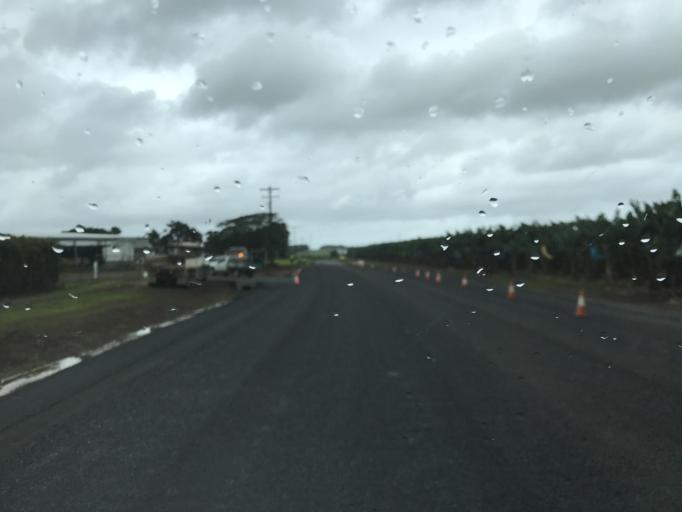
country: AU
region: Queensland
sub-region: Cassowary Coast
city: Innisfail
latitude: -17.5015
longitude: 145.9825
